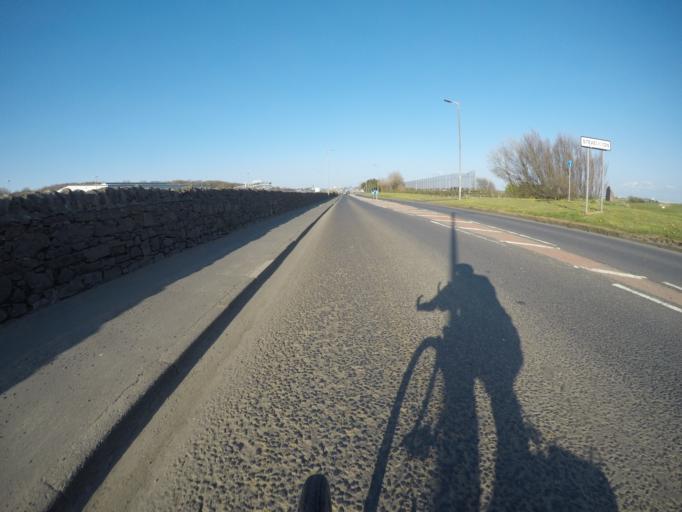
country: GB
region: Scotland
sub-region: North Ayrshire
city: Saltcoats
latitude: 55.6354
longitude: -4.7742
